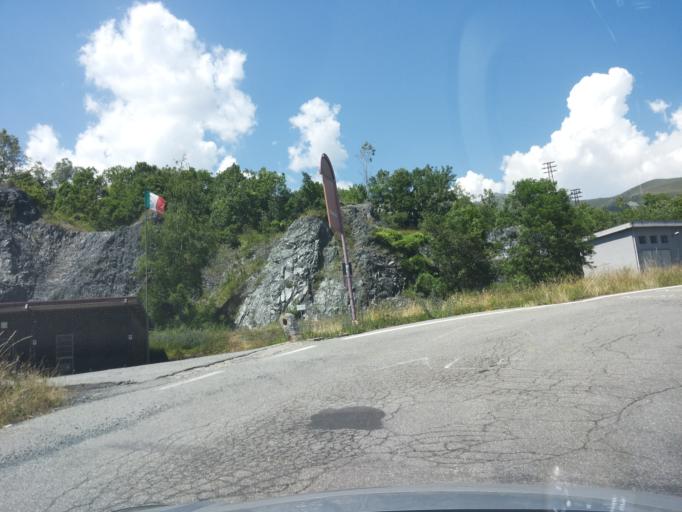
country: IT
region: Piedmont
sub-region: Provincia di Biella
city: Pollone
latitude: 45.5994
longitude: 8.0034
